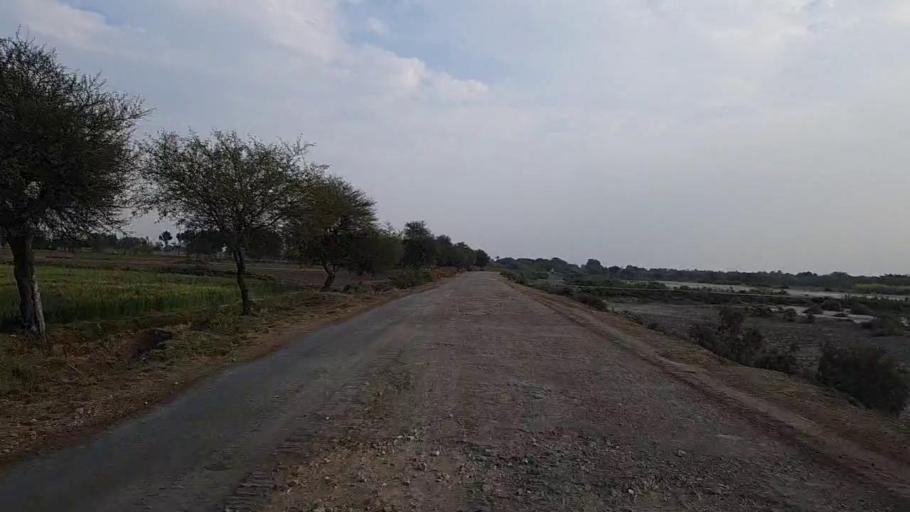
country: PK
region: Sindh
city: Pithoro
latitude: 25.4654
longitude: 69.2747
